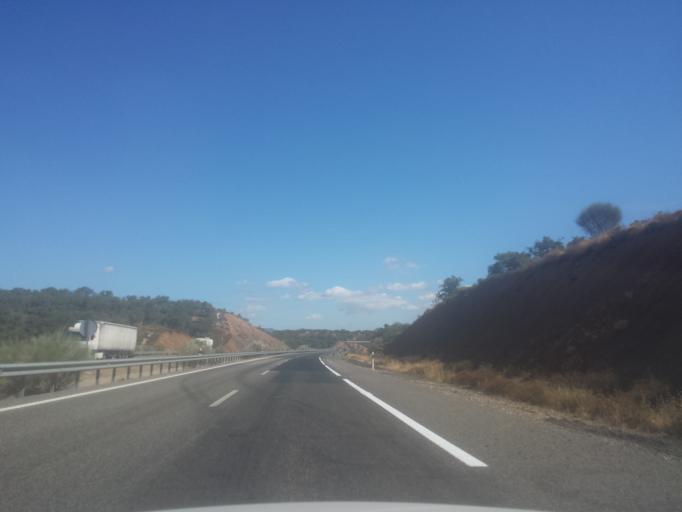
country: ES
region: Andalusia
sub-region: Provincia de Huelva
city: Santa Olalla del Cala
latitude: 37.8737
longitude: -6.2205
